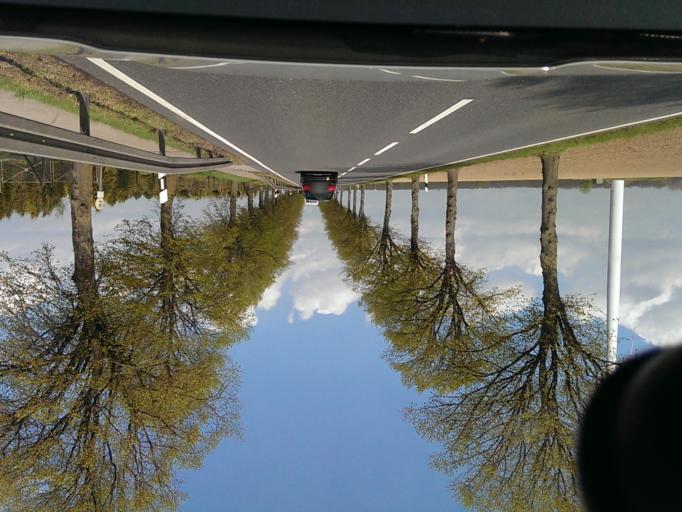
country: DE
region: Lower Saxony
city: Nordstemmen
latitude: 52.1935
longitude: 9.7464
